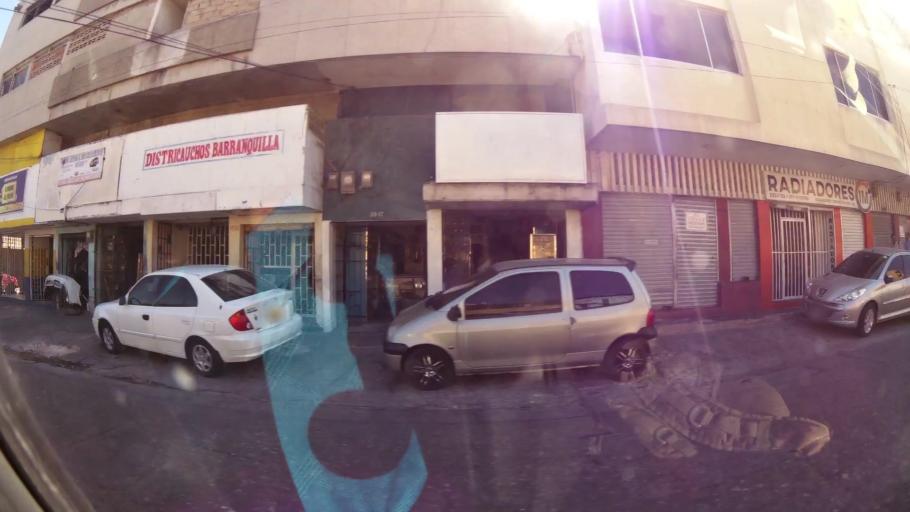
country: CO
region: Atlantico
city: Barranquilla
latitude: 10.9783
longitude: -74.7825
